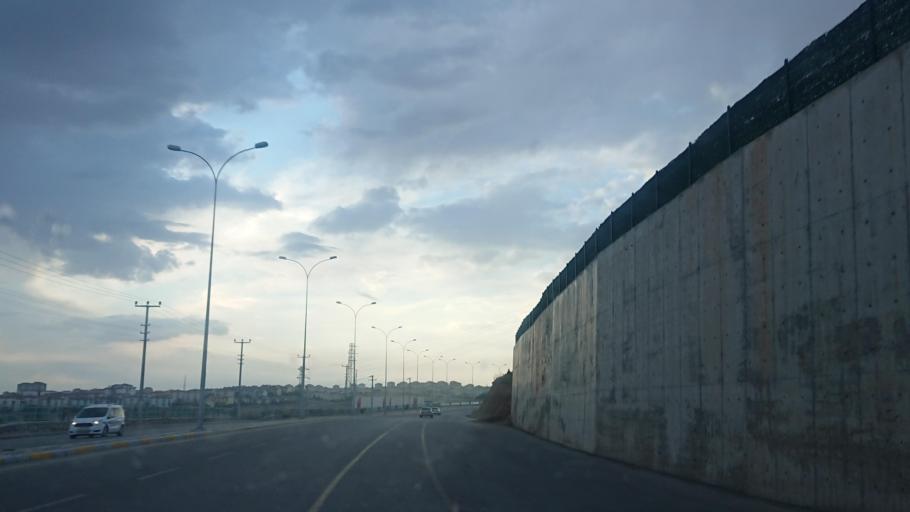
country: TR
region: Aksaray
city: Aksaray
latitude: 38.4042
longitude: 34.0141
